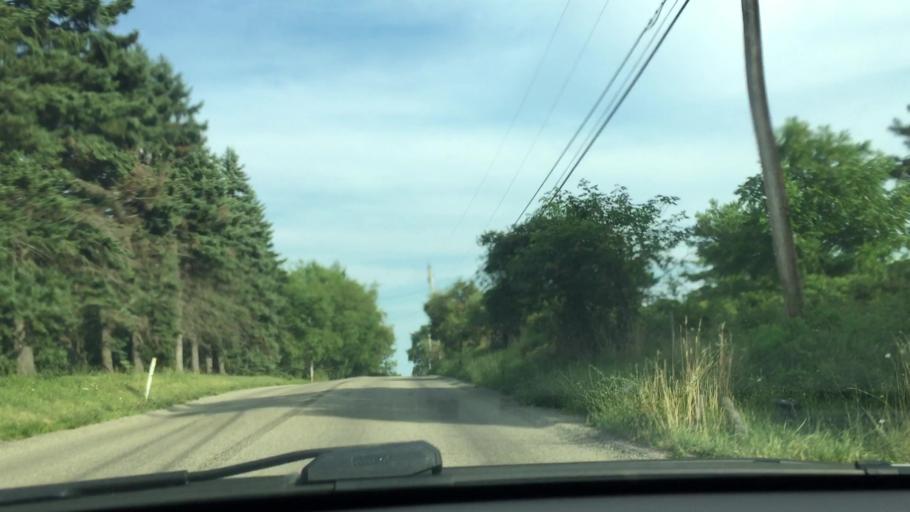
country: US
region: Pennsylvania
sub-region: Butler County
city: Seven Fields
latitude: 40.6809
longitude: -80.0732
